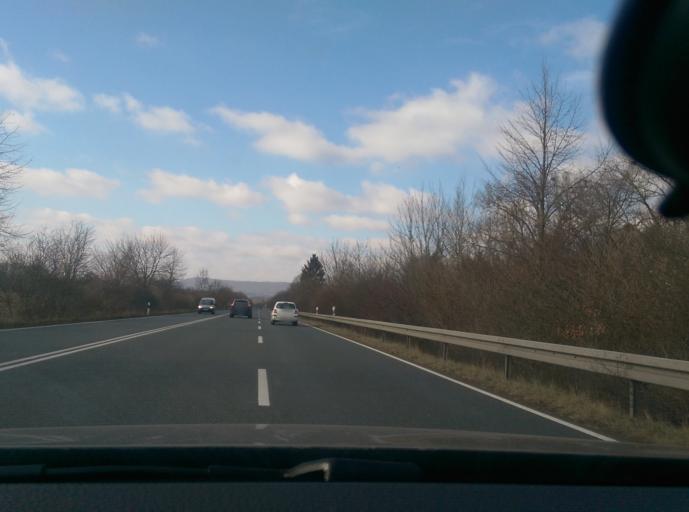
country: DE
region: Lower Saxony
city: Hessisch Oldendorf
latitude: 52.1527
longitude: 9.2798
